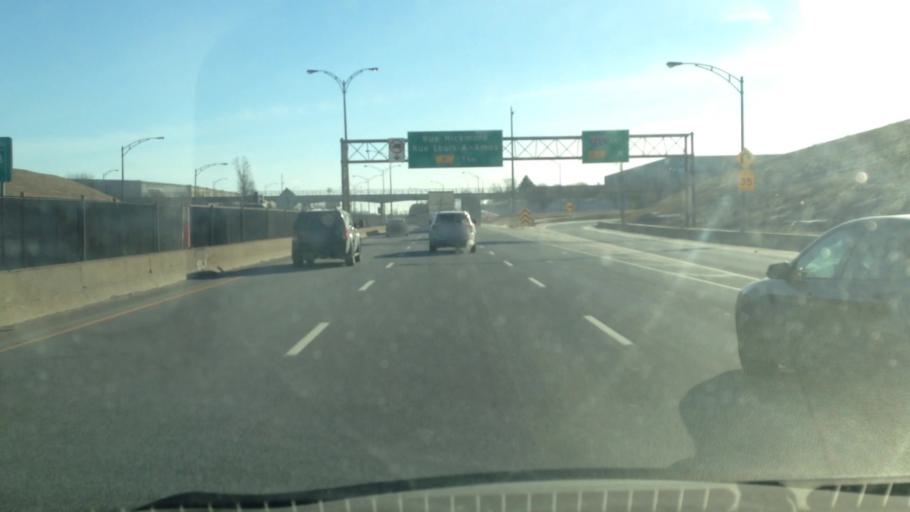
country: CA
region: Quebec
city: Cote-Saint-Luc
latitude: 45.4728
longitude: -73.7078
